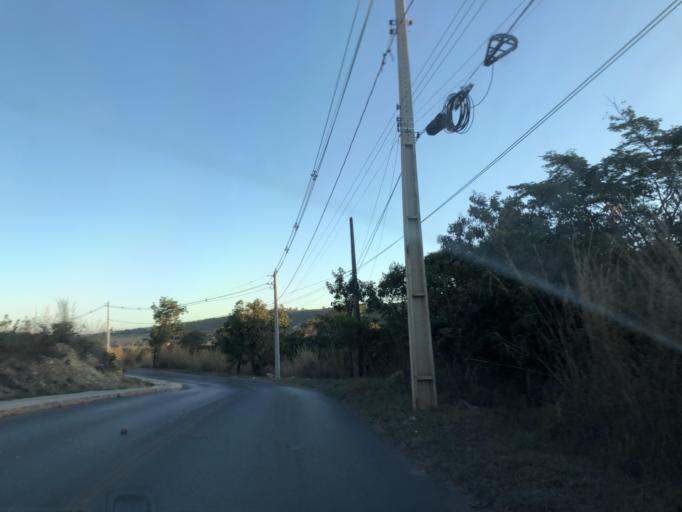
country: BR
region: Federal District
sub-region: Brasilia
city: Brasilia
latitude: -15.8690
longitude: -47.7828
